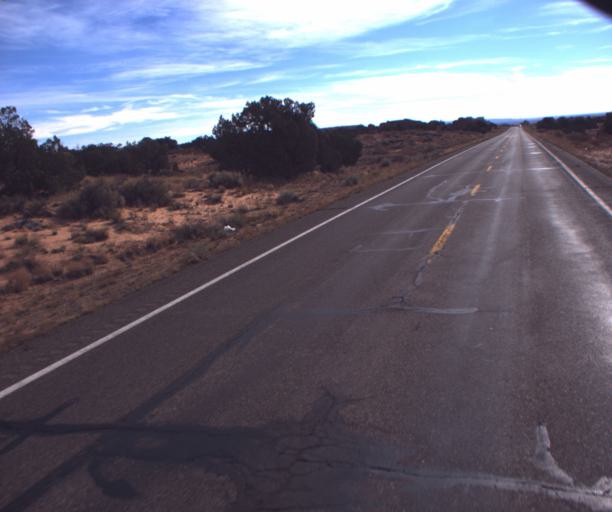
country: US
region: Arizona
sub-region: Coconino County
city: Kaibito
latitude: 36.6459
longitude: -111.2263
